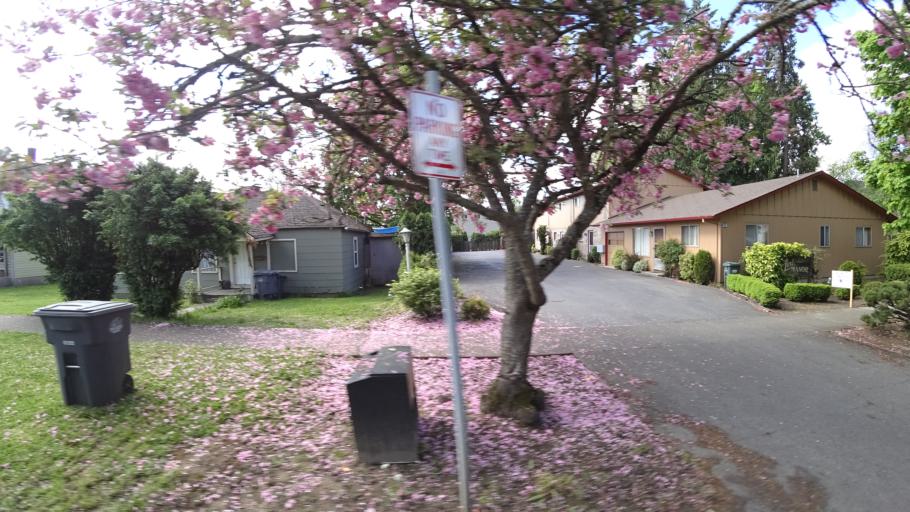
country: US
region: Oregon
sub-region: Washington County
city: Hillsboro
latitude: 45.5174
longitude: -122.9853
